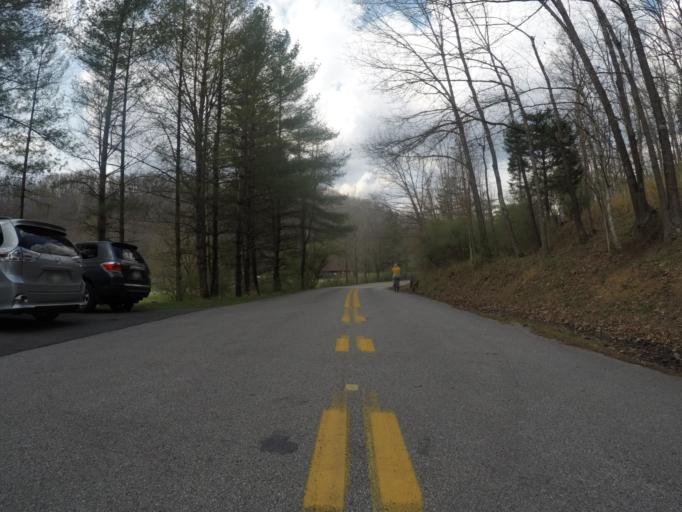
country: US
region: West Virginia
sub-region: Wayne County
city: Lavalette
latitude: 38.3086
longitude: -82.3572
